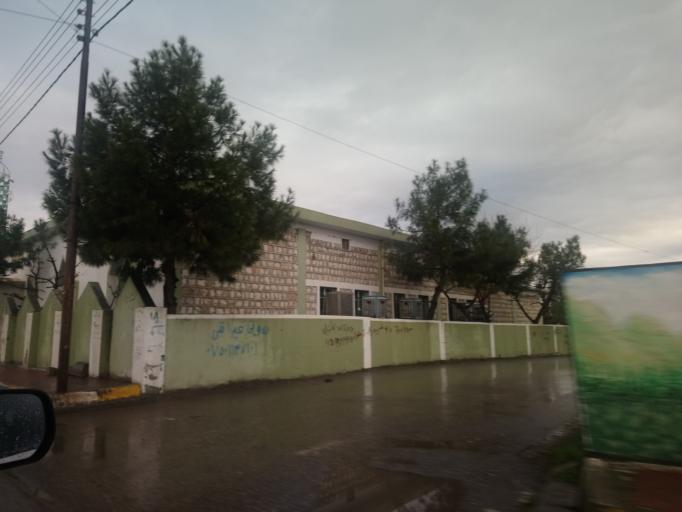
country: IQ
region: As Sulaymaniyah
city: Qeladize
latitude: 36.1850
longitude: 45.1182
